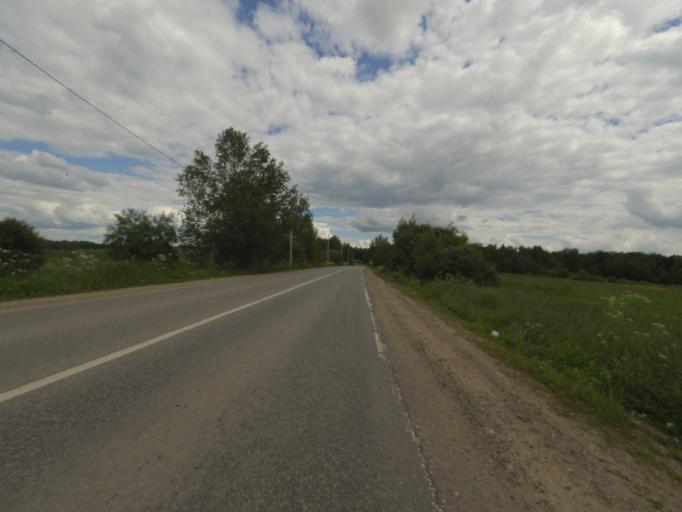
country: RU
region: Moskovskaya
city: Marfino
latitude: 56.0479
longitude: 37.5769
